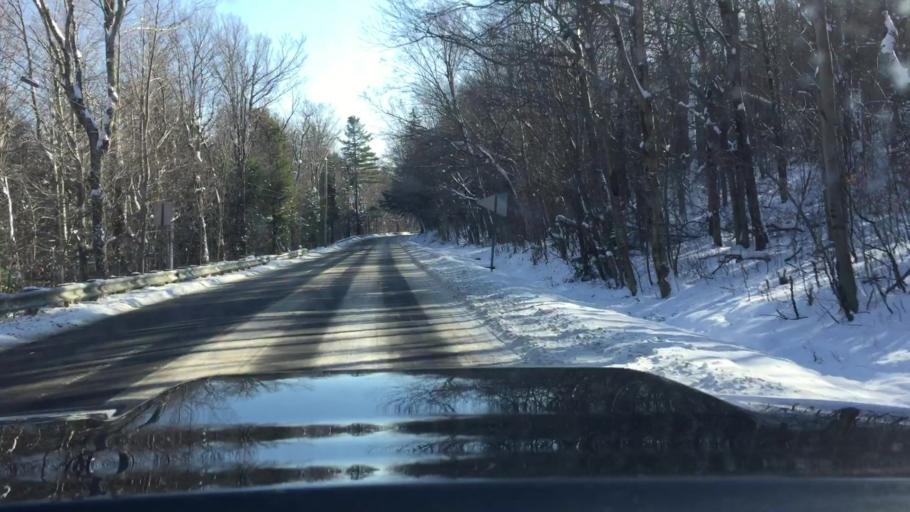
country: US
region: Massachusetts
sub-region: Berkshire County
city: Hinsdale
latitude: 42.4489
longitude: -72.9784
